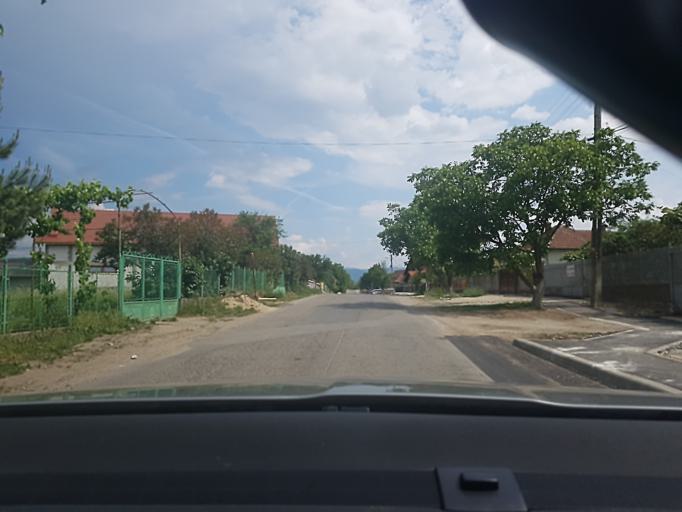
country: RO
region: Hunedoara
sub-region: Comuna Calan
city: Calan
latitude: 45.7241
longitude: 23.0208
